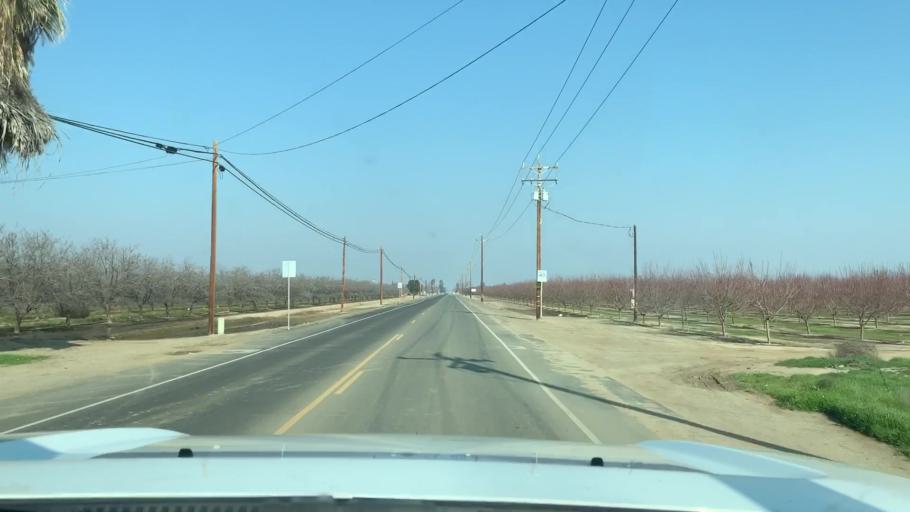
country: US
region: California
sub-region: Kern County
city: Shafter
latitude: 35.4816
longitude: -119.2785
